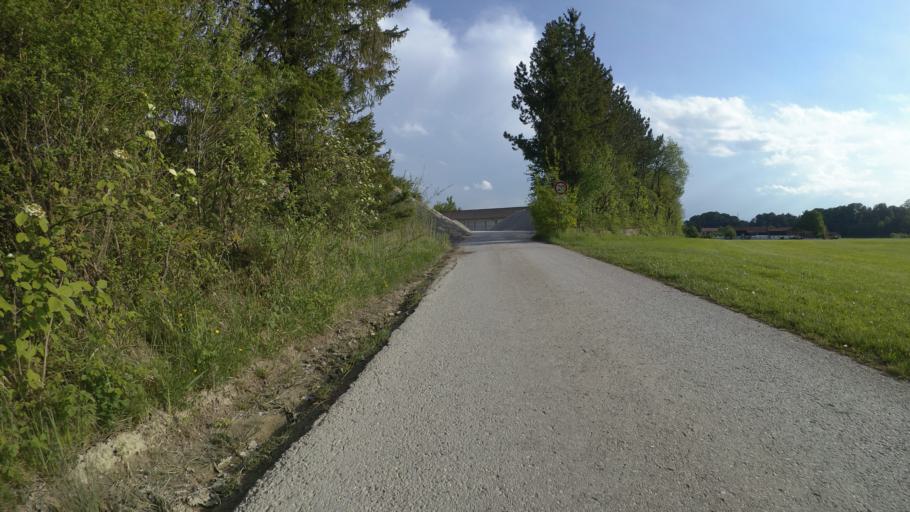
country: DE
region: Bavaria
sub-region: Upper Bavaria
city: Chieming
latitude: 47.8954
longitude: 12.5679
